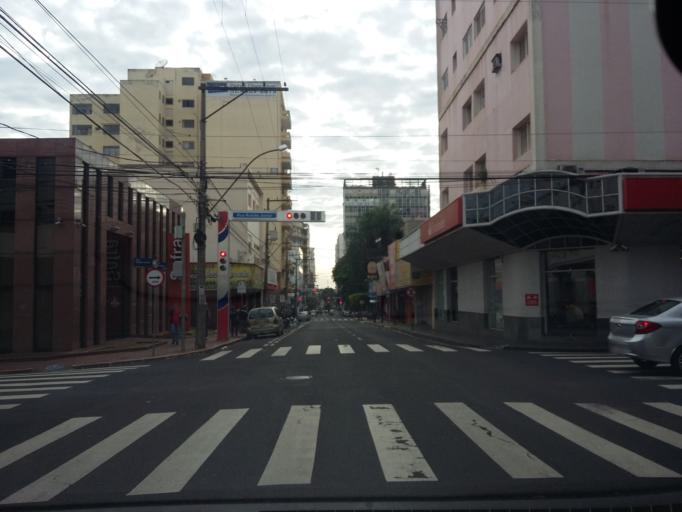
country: BR
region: Sao Paulo
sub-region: Sao Jose Do Rio Preto
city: Sao Jose do Rio Preto
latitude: -20.8141
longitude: -49.3836
